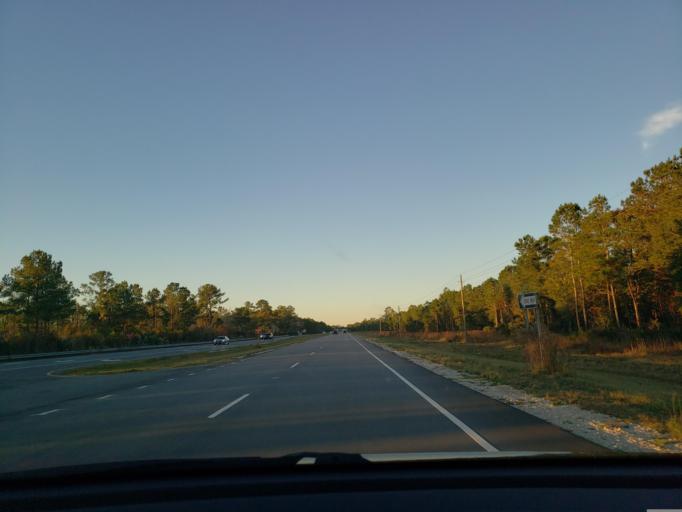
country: US
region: North Carolina
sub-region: Onslow County
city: Sneads Ferry
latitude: 34.5990
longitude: -77.4813
